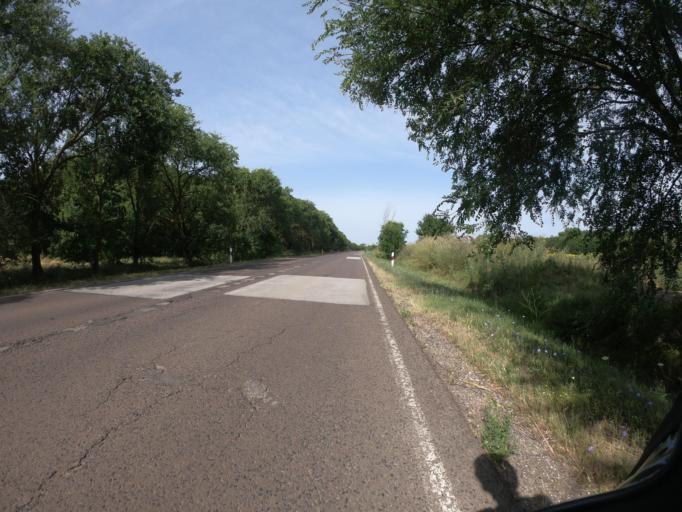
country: HU
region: Hajdu-Bihar
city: Egyek
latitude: 47.5936
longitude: 20.8420
